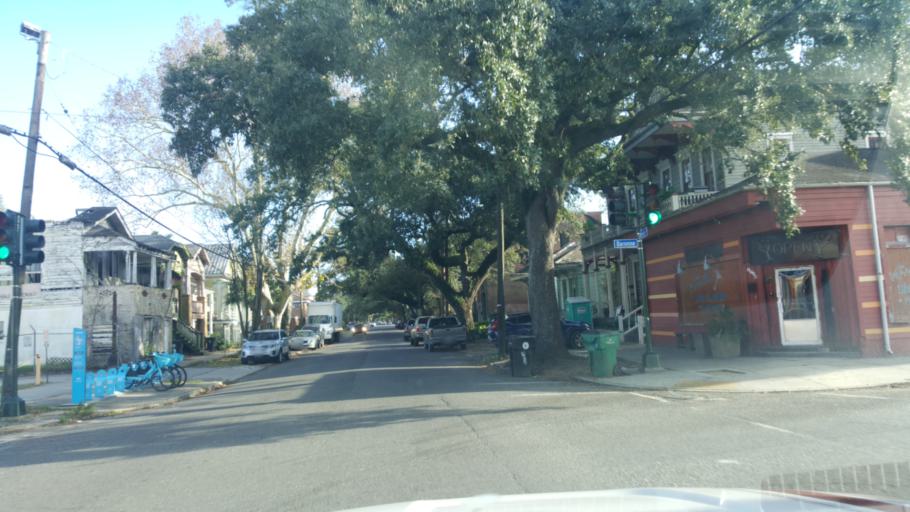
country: US
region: Louisiana
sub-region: Orleans Parish
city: New Orleans
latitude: 29.9329
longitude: -90.0873
